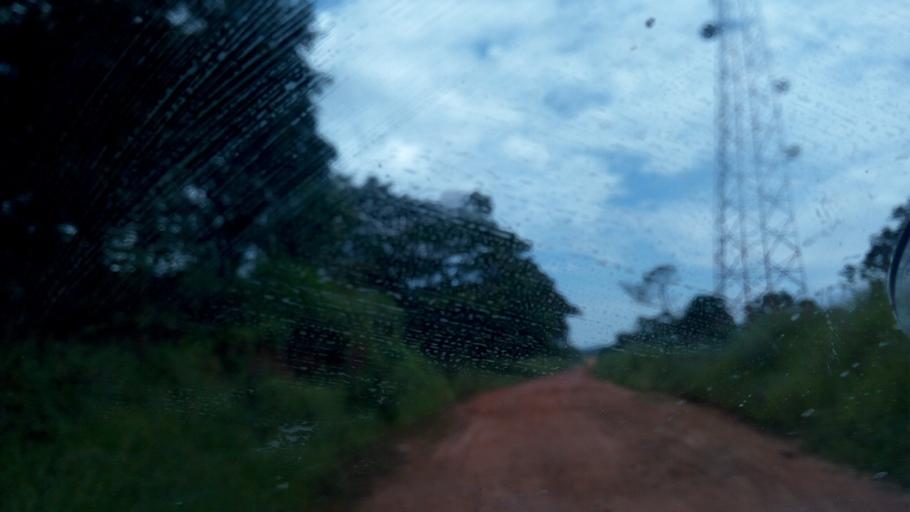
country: CD
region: Katanga
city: Kalemie
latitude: -5.2873
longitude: 28.8905
